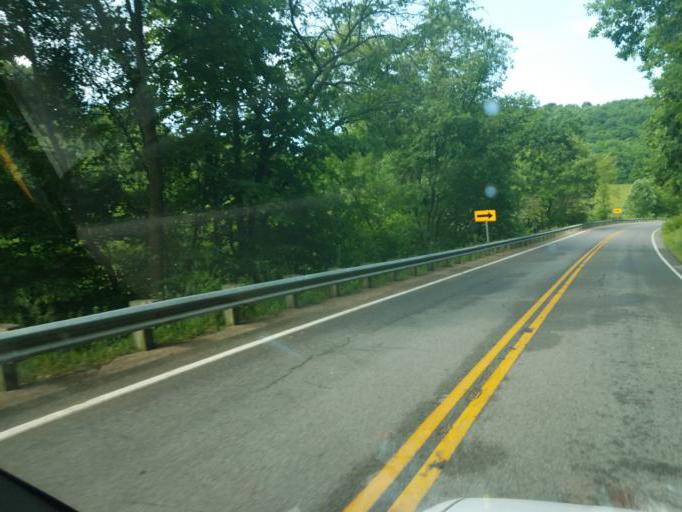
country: US
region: Wisconsin
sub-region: Vernon County
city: Hillsboro
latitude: 43.6747
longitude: -90.4946
